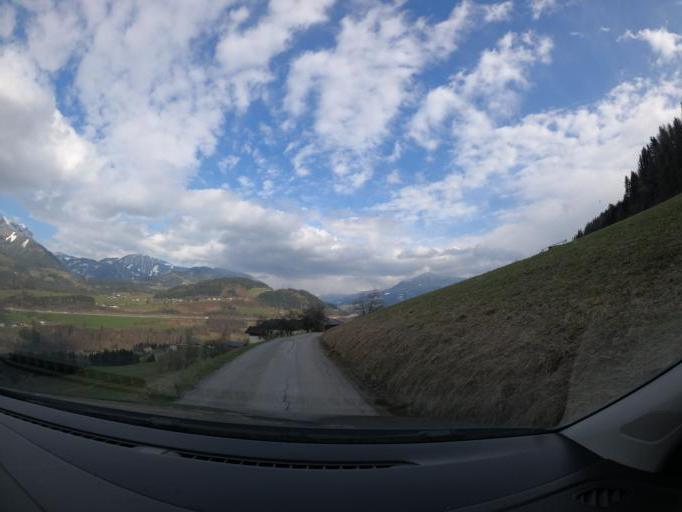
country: AT
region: Salzburg
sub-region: Politischer Bezirk Sankt Johann im Pongau
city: Pfarrwerfen
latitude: 47.4493
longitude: 13.1979
